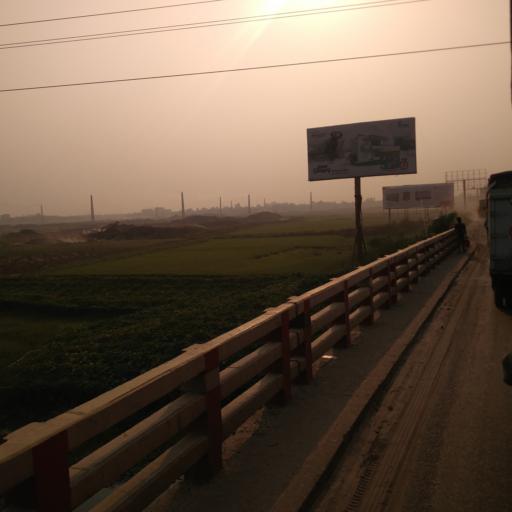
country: BD
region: Dhaka
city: Tungi
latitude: 23.8945
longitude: 90.3488
